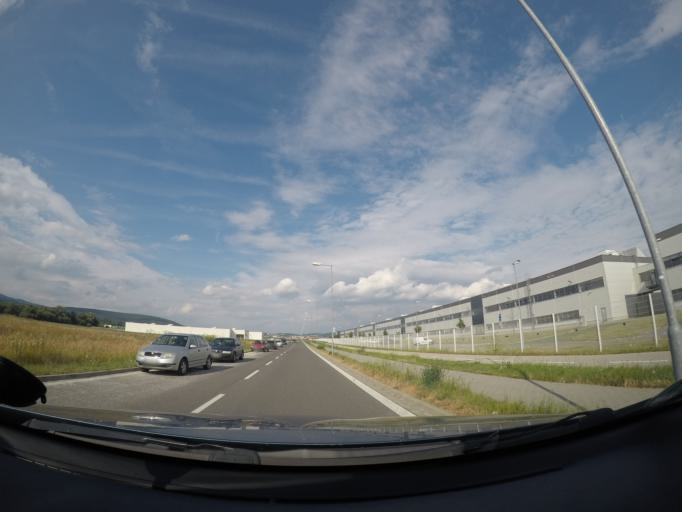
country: SK
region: Trenciansky
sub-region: Okres Trencin
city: Trencin
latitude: 48.8868
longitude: 17.9934
